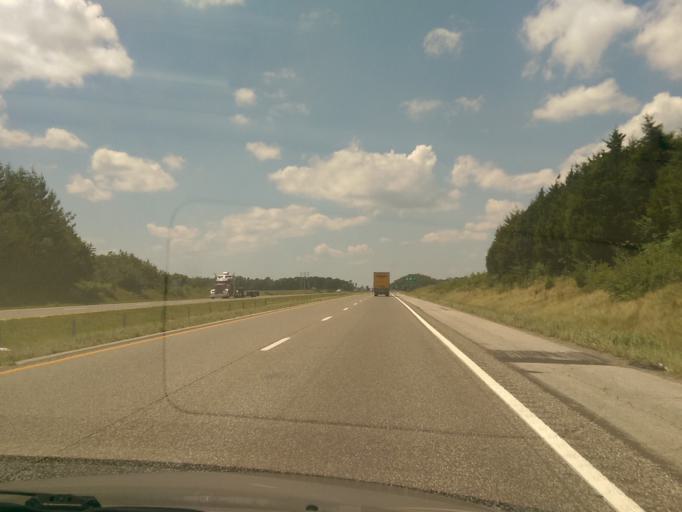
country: US
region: Missouri
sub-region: Boone County
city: Columbia
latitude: 38.9736
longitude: -92.4890
